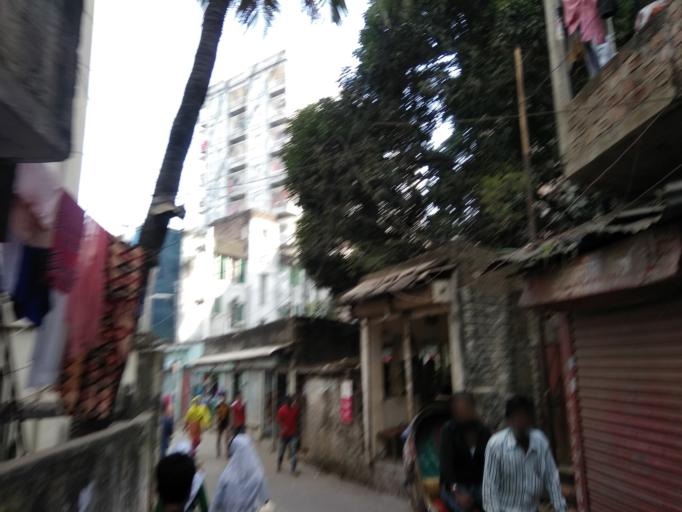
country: BD
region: Dhaka
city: Azimpur
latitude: 23.7742
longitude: 90.3582
